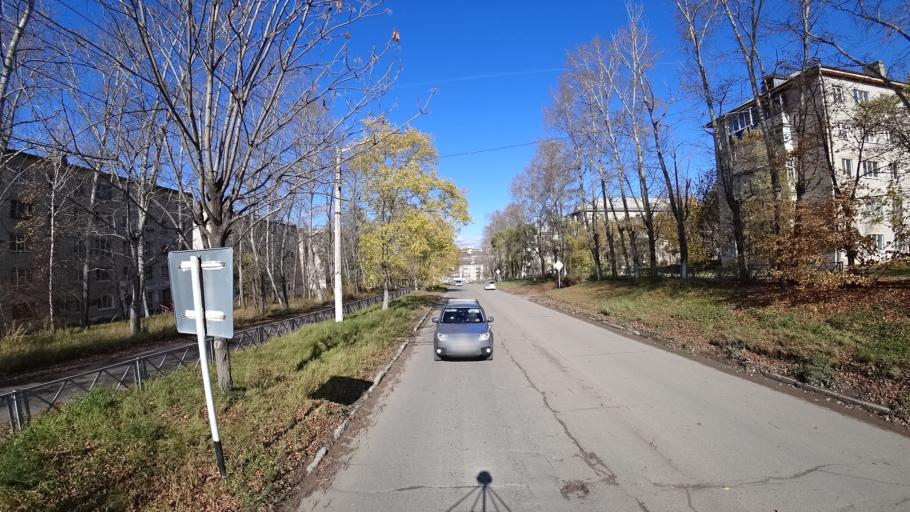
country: RU
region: Khabarovsk Krai
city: Amursk
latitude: 50.2203
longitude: 136.9032
